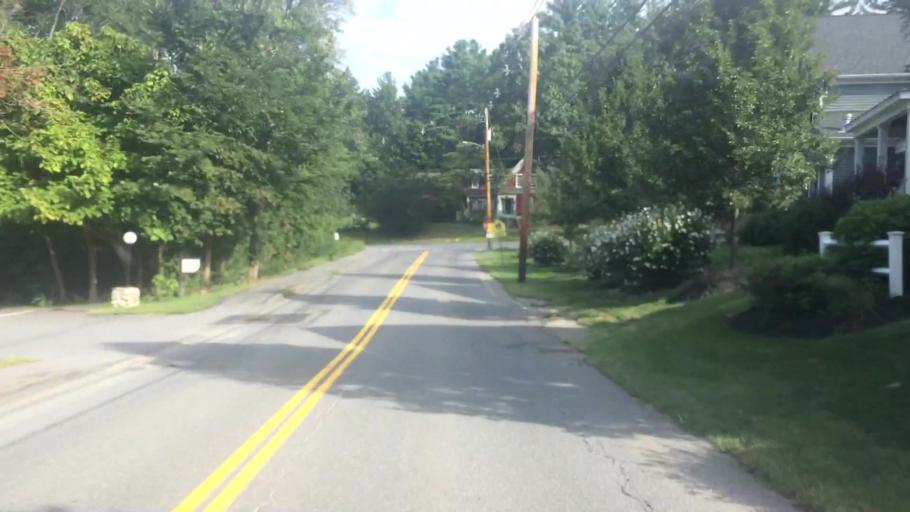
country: US
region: Massachusetts
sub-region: Middlesex County
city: Acton
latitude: 42.4740
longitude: -71.4592
